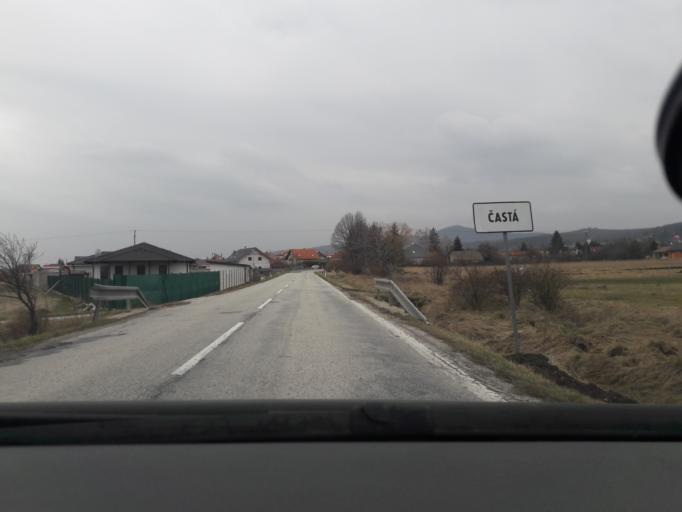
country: SK
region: Bratislavsky
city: Modra
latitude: 48.4021
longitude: 17.3705
